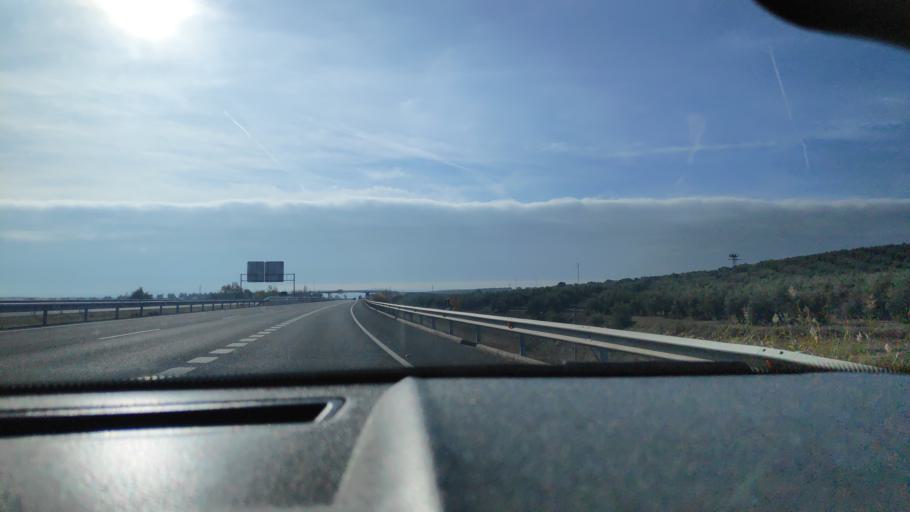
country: ES
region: Andalusia
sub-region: Provincia de Jaen
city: Bailen
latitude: 38.0953
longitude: -3.7396
